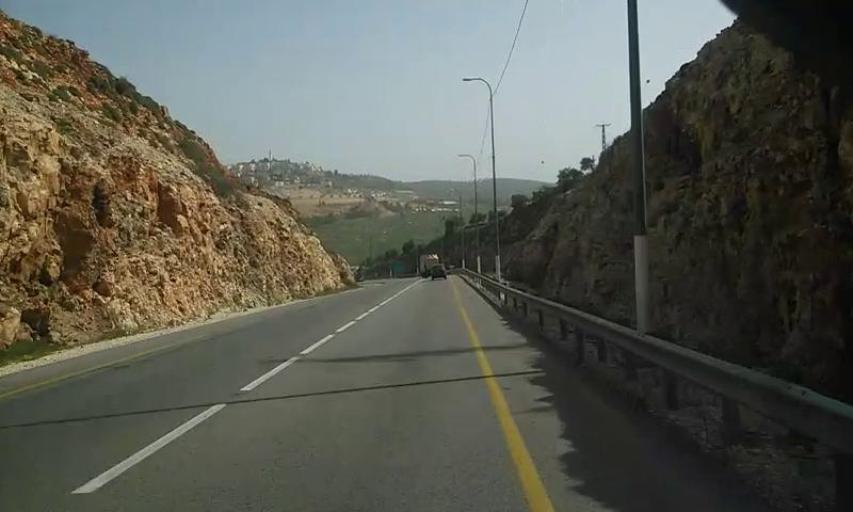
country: PS
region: West Bank
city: Turmus`ayya
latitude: 32.0484
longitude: 35.2898
